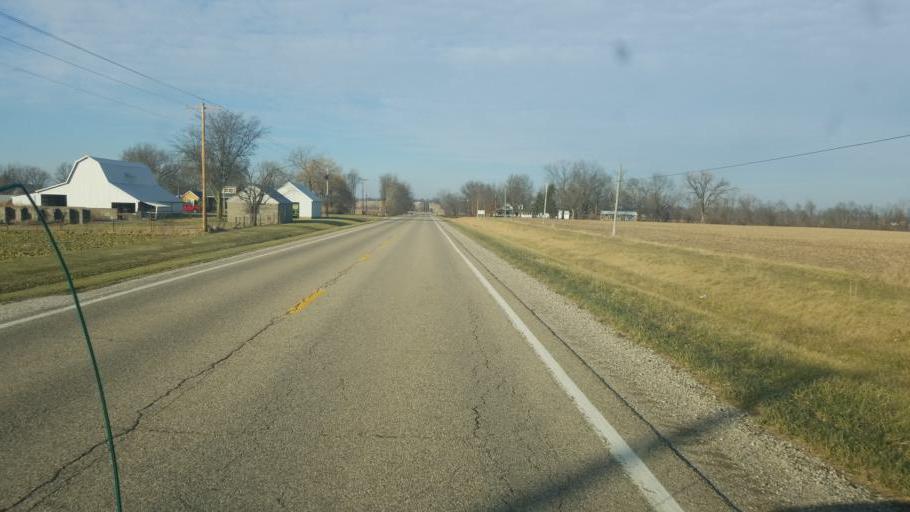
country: US
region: Illinois
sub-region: Lawrence County
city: Lawrenceville
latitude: 38.6349
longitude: -87.6942
